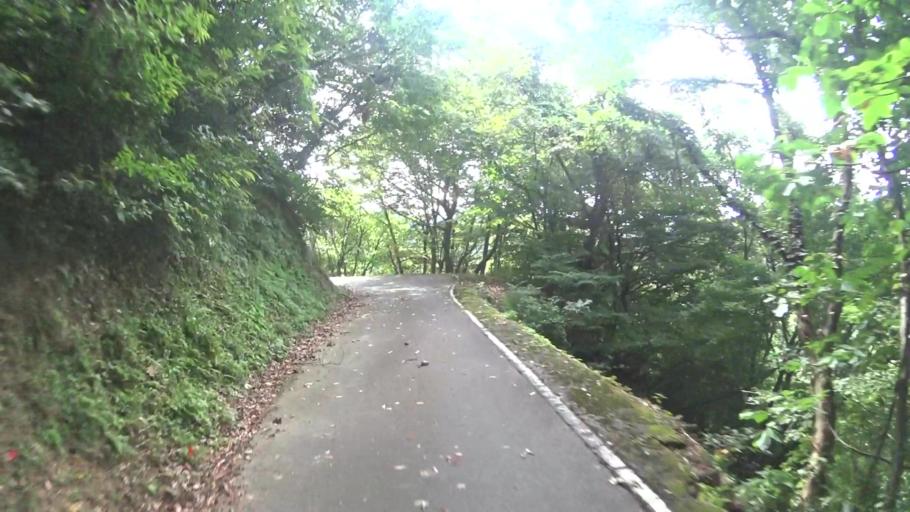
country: JP
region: Kyoto
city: Miyazu
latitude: 35.7374
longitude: 135.1962
